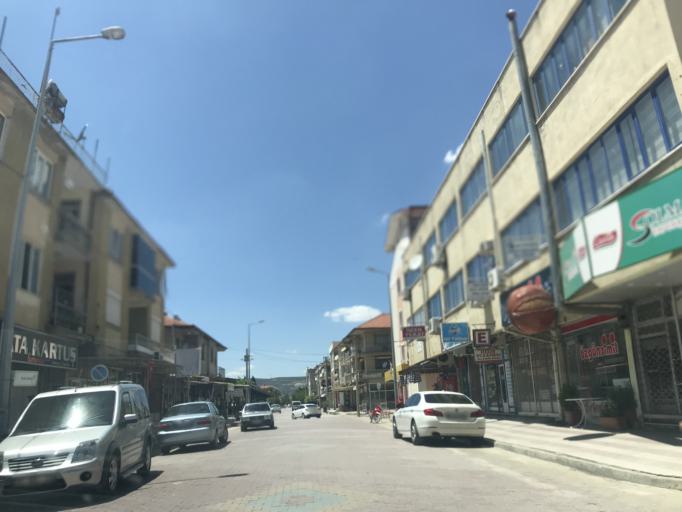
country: TR
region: Denizli
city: Civril
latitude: 38.3009
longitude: 29.7400
